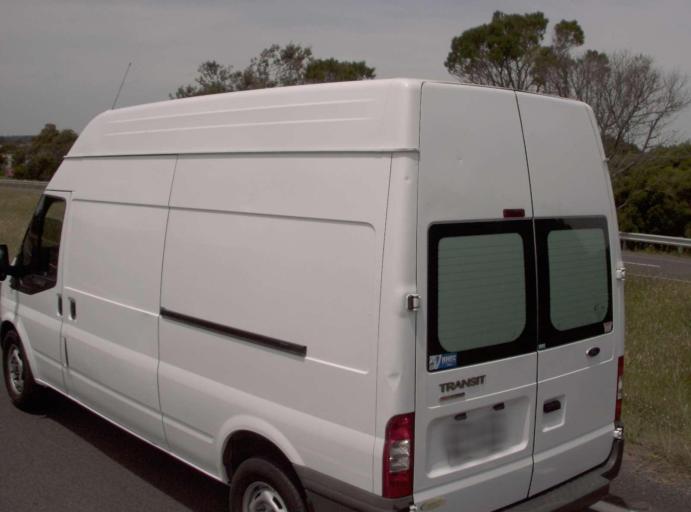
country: AU
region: Victoria
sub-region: Mornington Peninsula
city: Safety Beach
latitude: -38.3290
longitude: 144.9903
